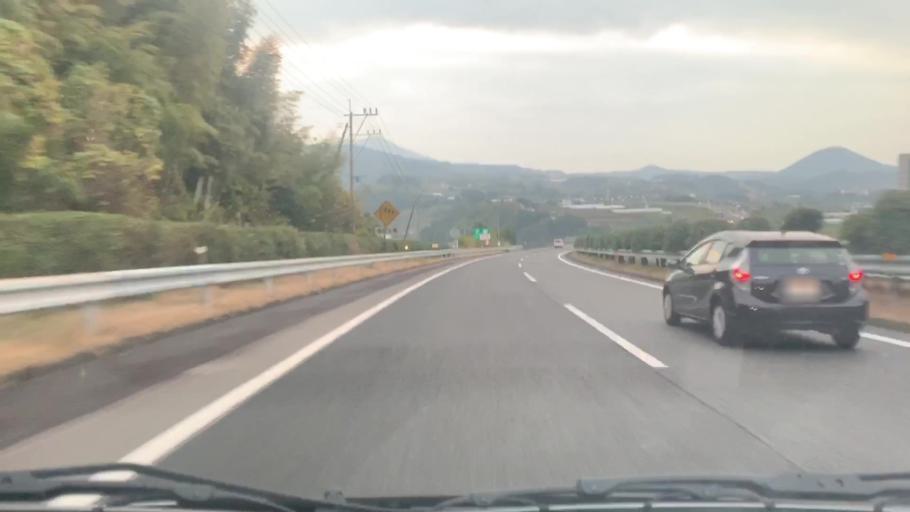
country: JP
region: Nagasaki
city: Omura
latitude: 33.0260
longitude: 129.9388
